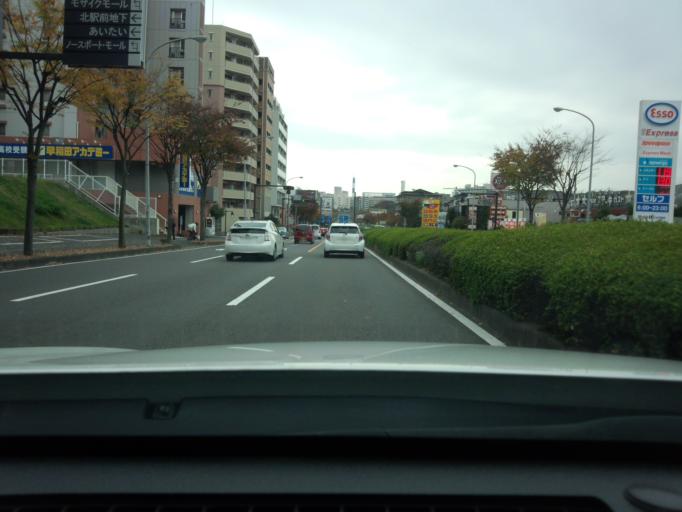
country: JP
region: Tokyo
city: Chofugaoka
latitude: 35.5540
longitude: 139.5764
